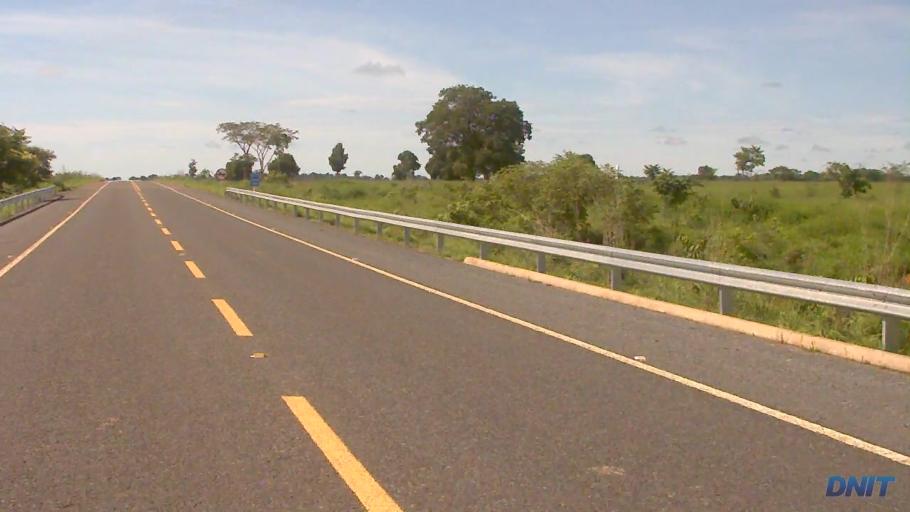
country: BR
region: Goias
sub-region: Sao Miguel Do Araguaia
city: Sao Miguel do Araguaia
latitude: -13.3805
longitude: -50.1409
